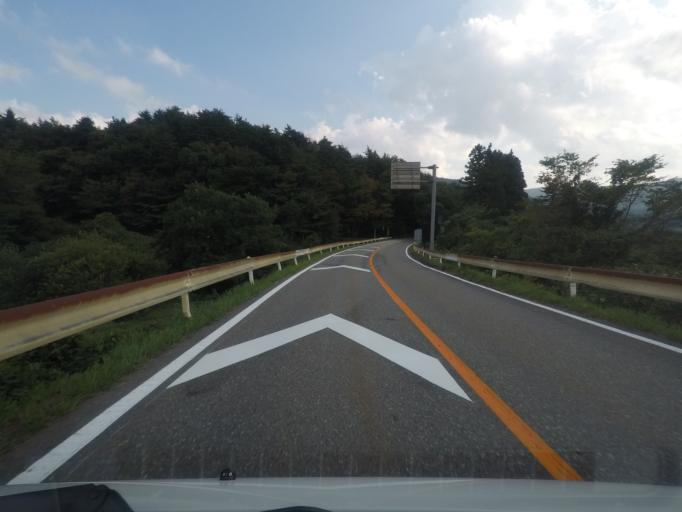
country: JP
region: Fukushima
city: Funehikimachi-funehiki
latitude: 37.5652
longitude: 140.7439
